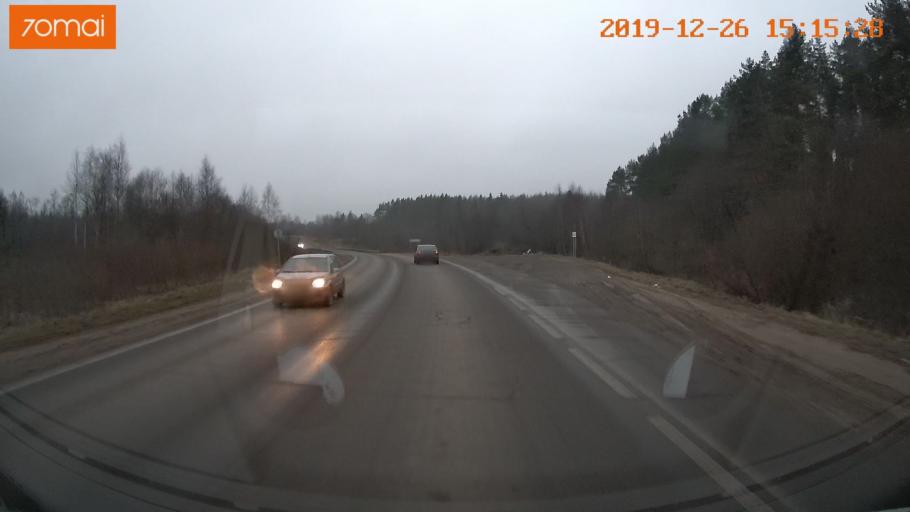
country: RU
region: Jaroslavl
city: Rybinsk
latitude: 58.0965
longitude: 38.8745
